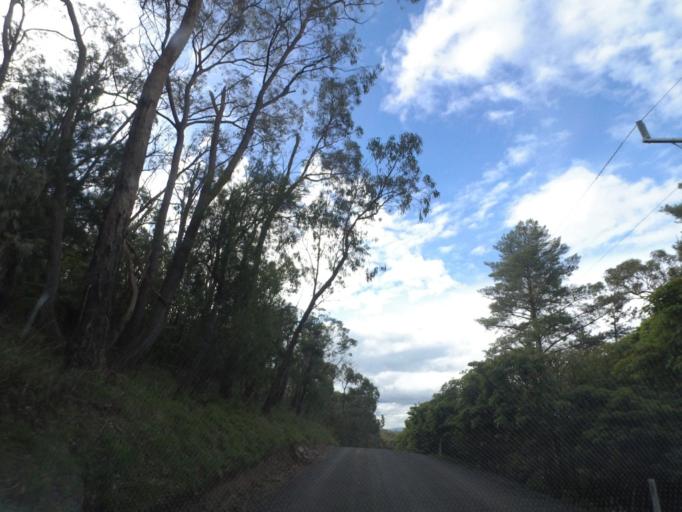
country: AU
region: Victoria
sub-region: Yarra Ranges
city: Mount Evelyn
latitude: -37.7666
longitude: 145.4082
